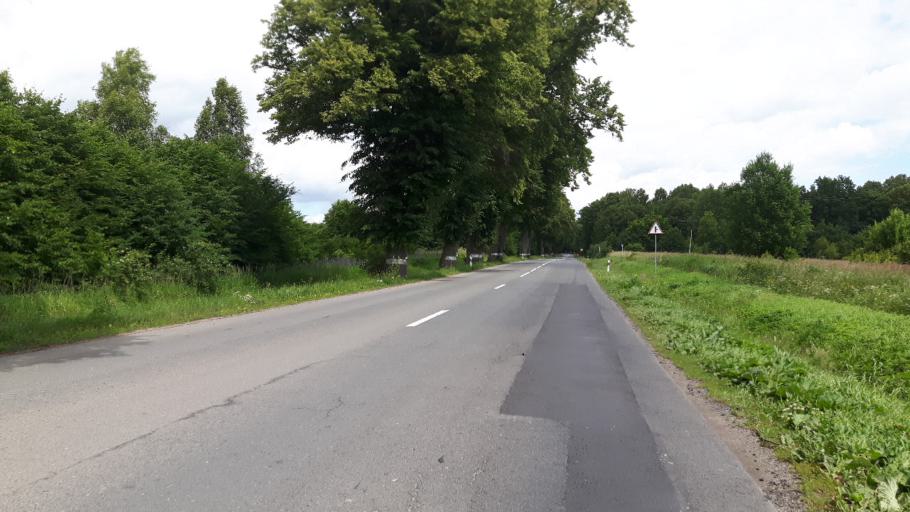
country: RU
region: Kaliningrad
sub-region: Gorod Kaliningrad
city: Kaliningrad
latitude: 54.8231
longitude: 20.4258
